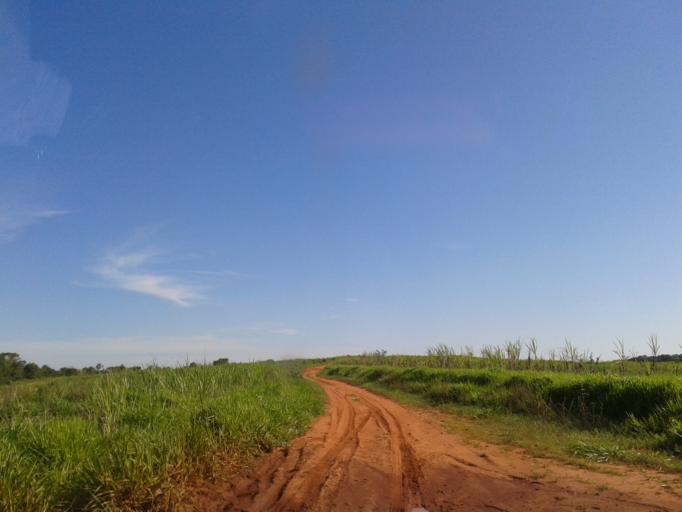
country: BR
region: Minas Gerais
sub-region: Santa Vitoria
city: Santa Vitoria
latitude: -19.0998
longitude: -49.9907
